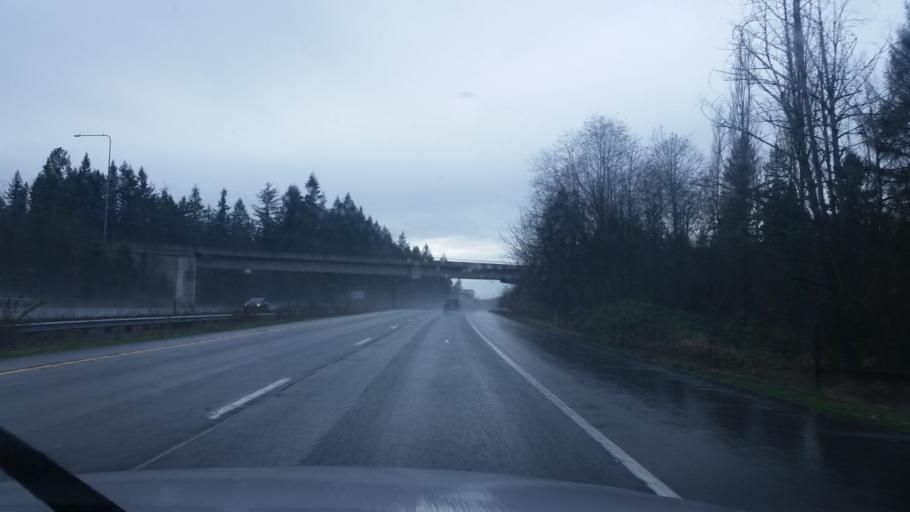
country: US
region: Washington
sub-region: King County
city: Hobart
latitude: 47.4231
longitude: -121.9966
